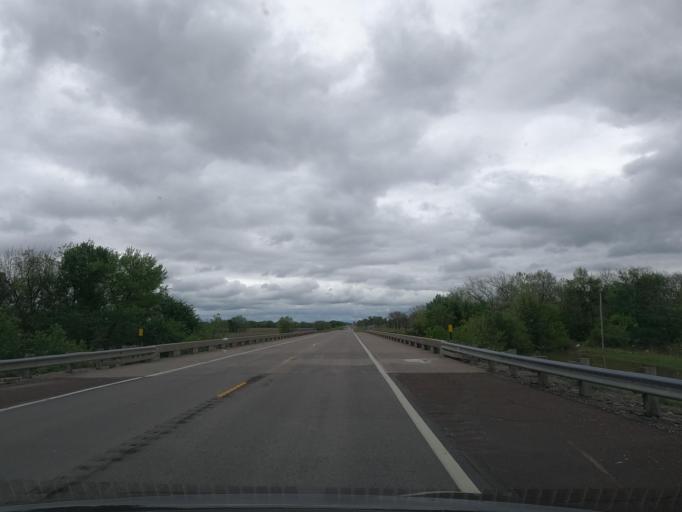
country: US
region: Kansas
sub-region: Labette County
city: Parsons
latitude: 37.3401
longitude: -95.1062
